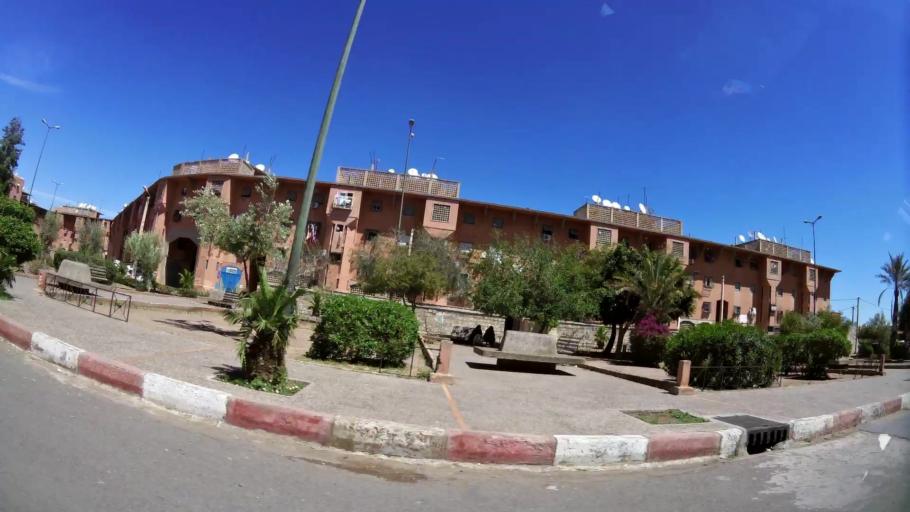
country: MA
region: Marrakech-Tensift-Al Haouz
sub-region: Marrakech
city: Marrakesh
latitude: 31.6341
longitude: -8.0644
